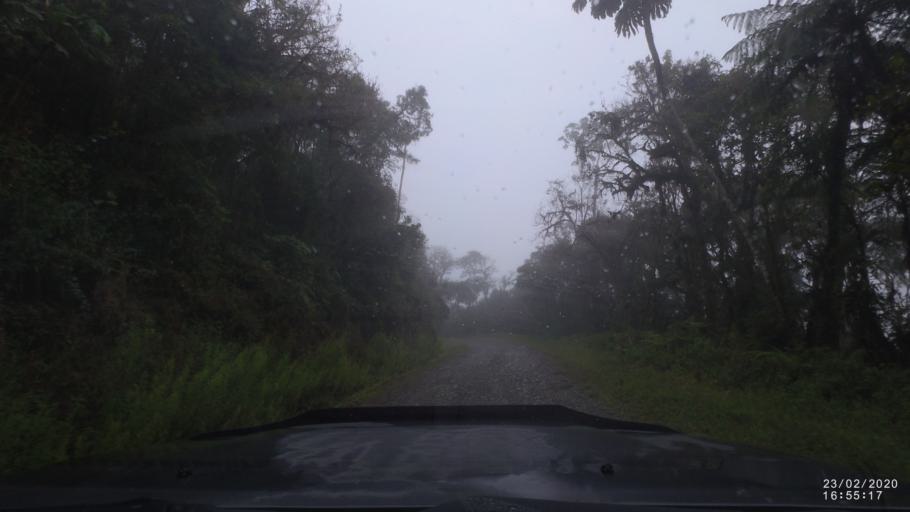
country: BO
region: Cochabamba
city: Colomi
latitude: -17.1017
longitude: -65.9816
